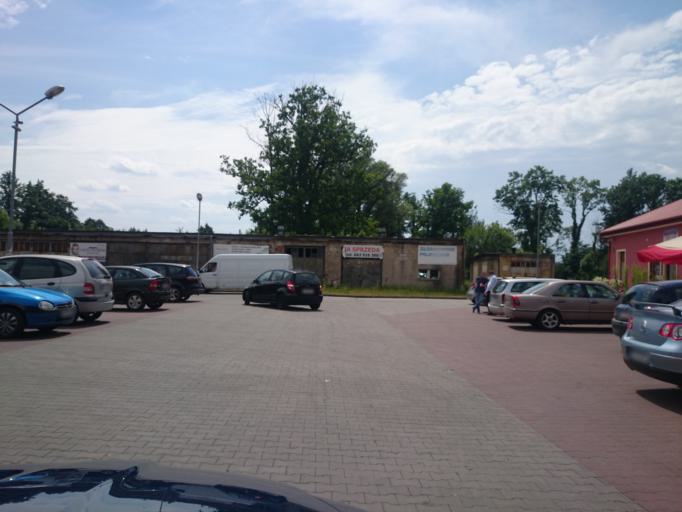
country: PL
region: West Pomeranian Voivodeship
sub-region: Powiat gryfinski
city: Chojna
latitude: 52.9595
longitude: 14.4341
